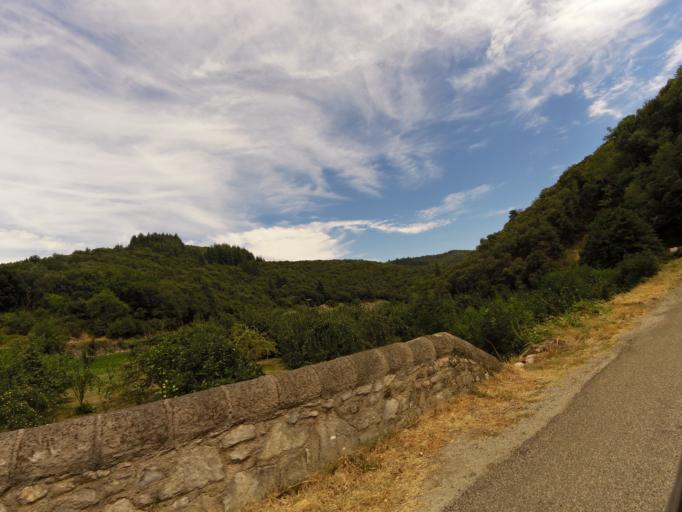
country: FR
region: Languedoc-Roussillon
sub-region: Departement du Gard
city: Le Vigan
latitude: 44.0085
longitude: 3.6487
